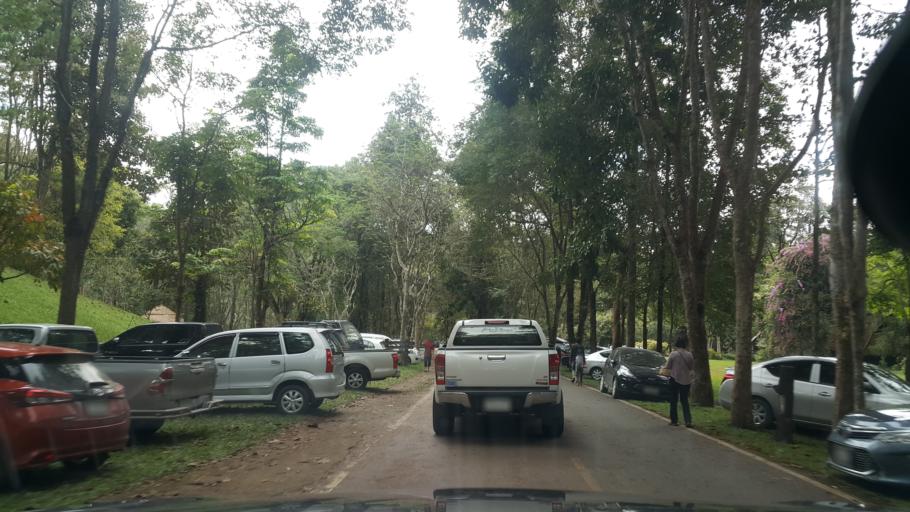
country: TH
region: Lampang
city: Mueang Pan
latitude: 18.8343
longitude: 99.4702
